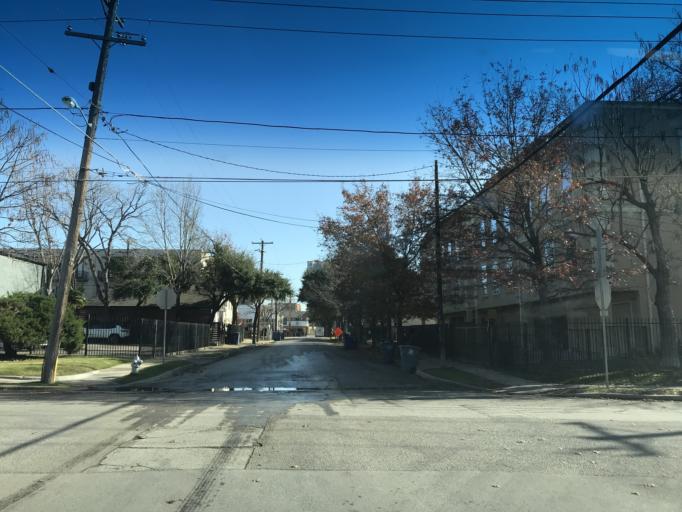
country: US
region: Texas
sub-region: Dallas County
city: Dallas
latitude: 32.8085
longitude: -96.8128
